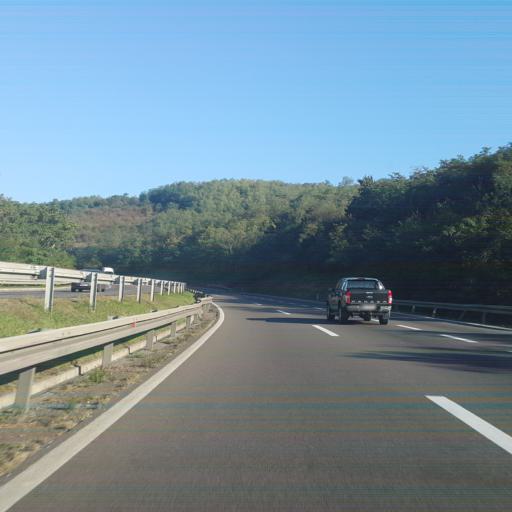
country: RS
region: Central Serbia
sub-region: Belgrade
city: Zvezdara
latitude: 44.7396
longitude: 20.5451
